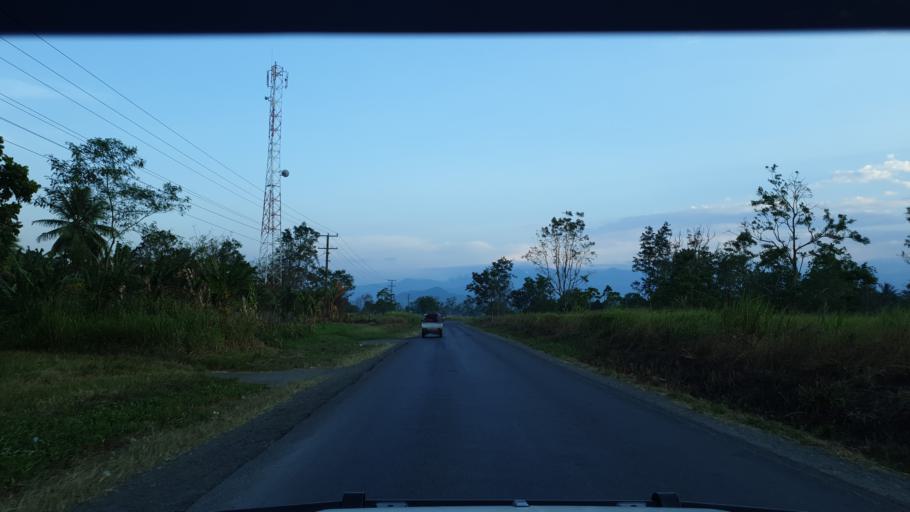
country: PG
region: Morobe
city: Lae
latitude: -6.5835
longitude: 146.7739
